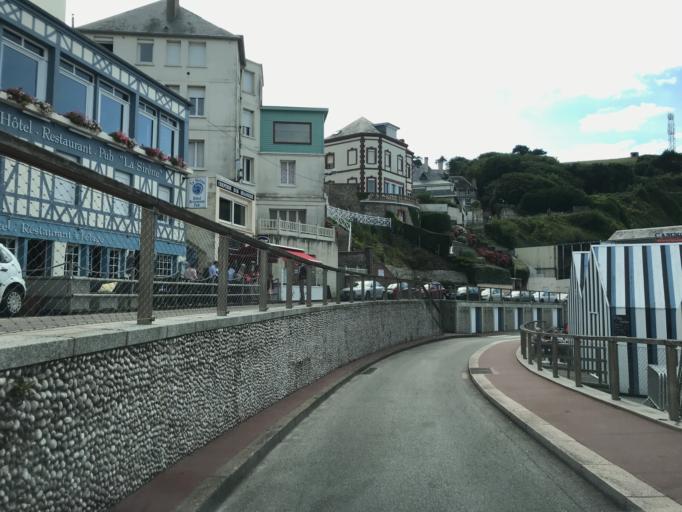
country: FR
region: Haute-Normandie
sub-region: Departement de la Seine-Maritime
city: Yport
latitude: 49.7394
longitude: 0.3098
